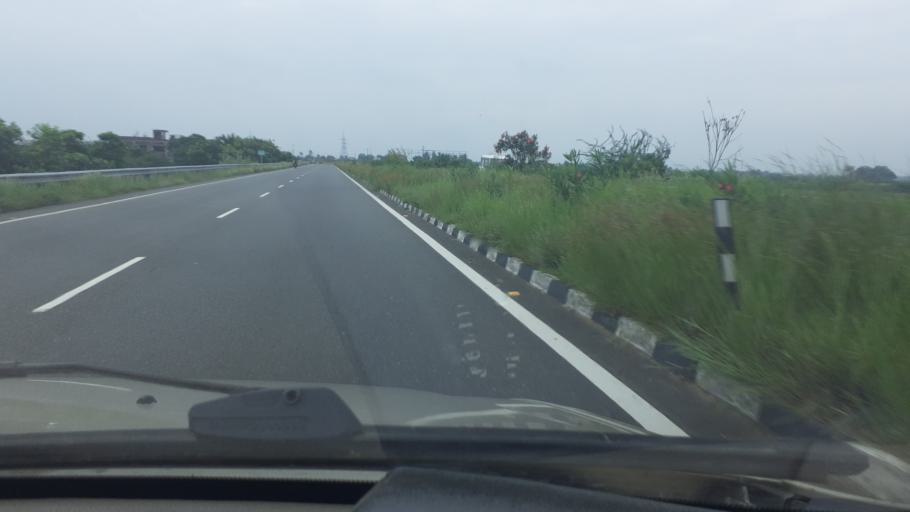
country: IN
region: Tamil Nadu
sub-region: Madurai
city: Tirupparangunram
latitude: 9.8362
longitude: 77.9936
